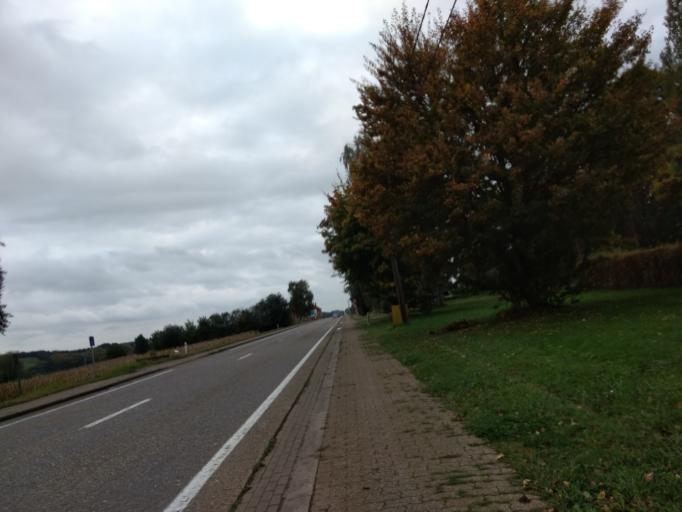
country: BE
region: Flanders
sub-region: Provincie Vlaams-Brabant
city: Bekkevoort
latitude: 50.9401
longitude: 4.9921
